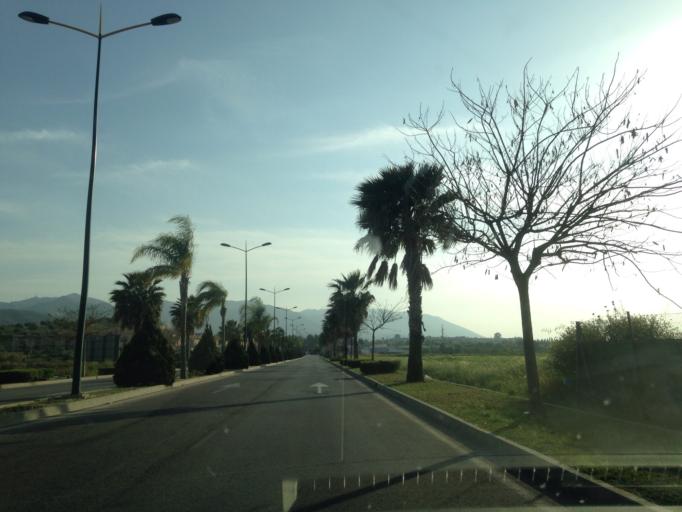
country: ES
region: Andalusia
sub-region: Provincia de Malaga
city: Alhaurin de la Torre
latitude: 36.6733
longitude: -4.5510
